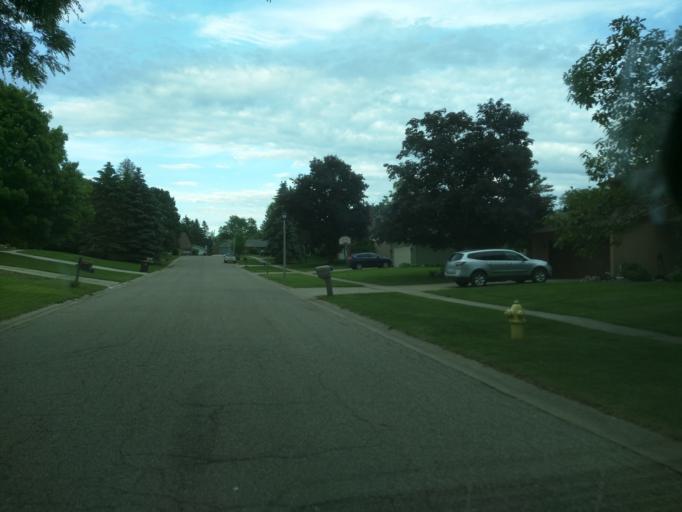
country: US
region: Michigan
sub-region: Eaton County
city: Waverly
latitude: 42.7505
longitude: -84.6200
